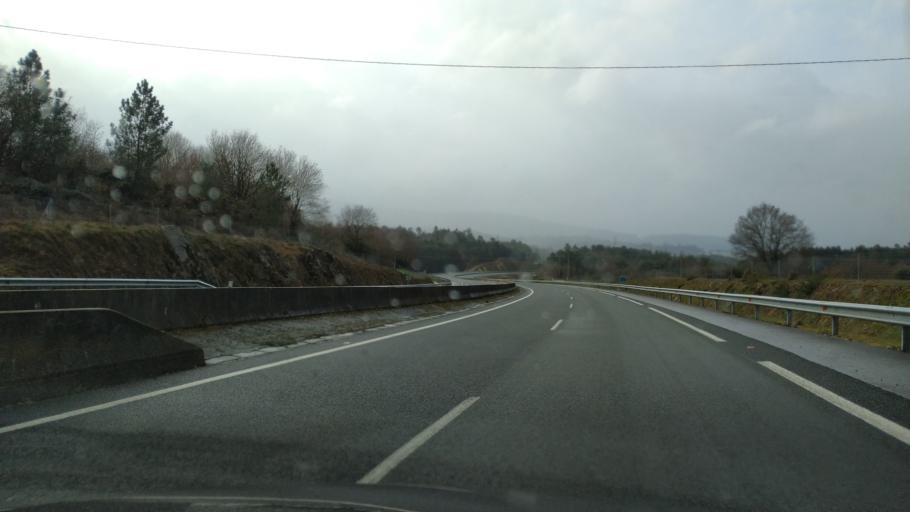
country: ES
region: Galicia
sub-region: Provincia de Pontevedra
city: Silleda
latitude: 42.7187
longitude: -8.2632
